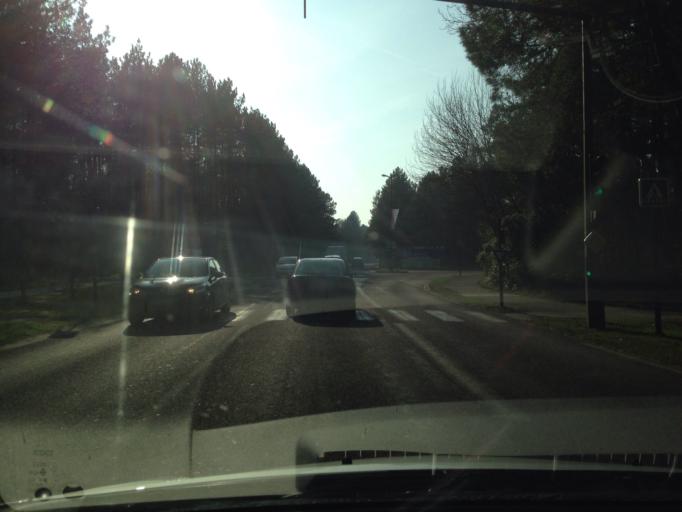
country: FR
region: Nord-Pas-de-Calais
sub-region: Departement du Pas-de-Calais
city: Etaples
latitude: 50.5082
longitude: 1.6123
